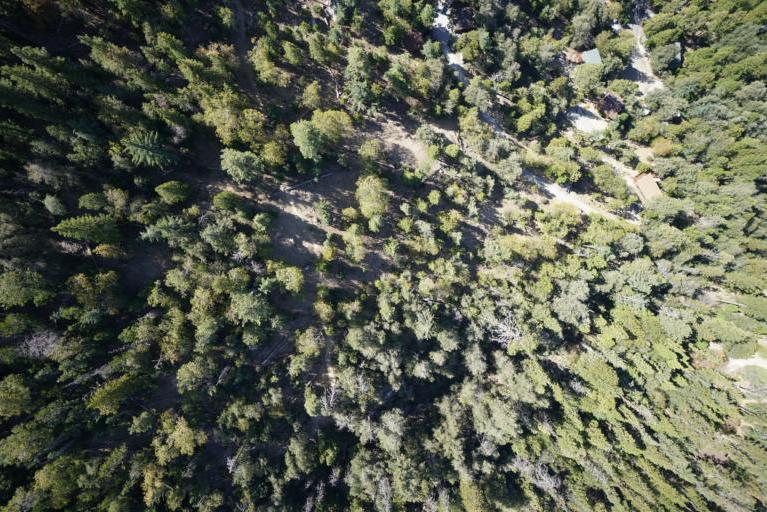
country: US
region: California
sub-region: Riverside County
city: Idyllwild
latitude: 33.7487
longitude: -116.6942
